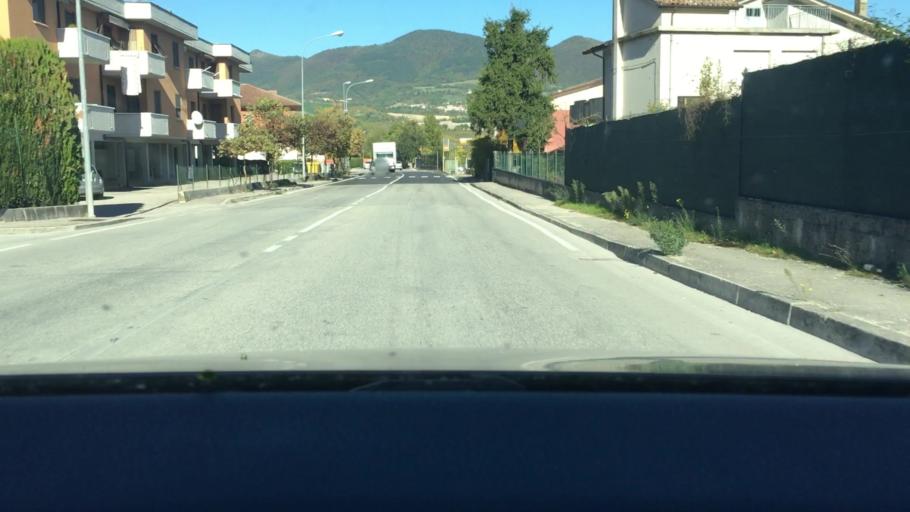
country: IT
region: The Marches
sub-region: Provincia di Ancona
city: Fabriano
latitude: 43.3497
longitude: 12.9150
